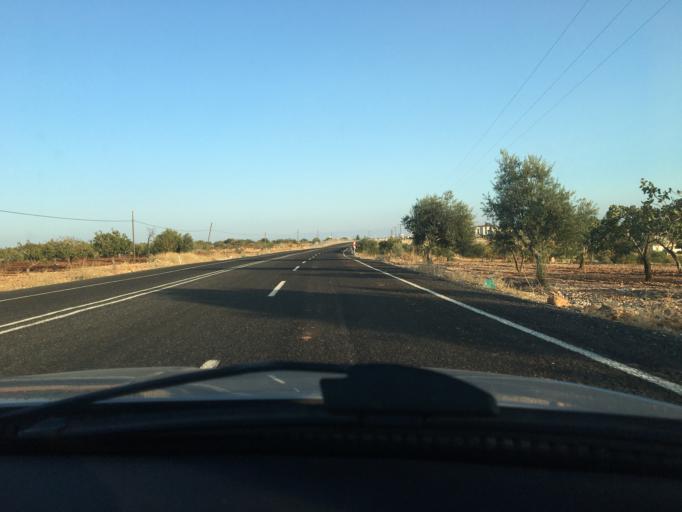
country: TR
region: Sanliurfa
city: Halfeti
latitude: 37.2440
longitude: 37.8989
